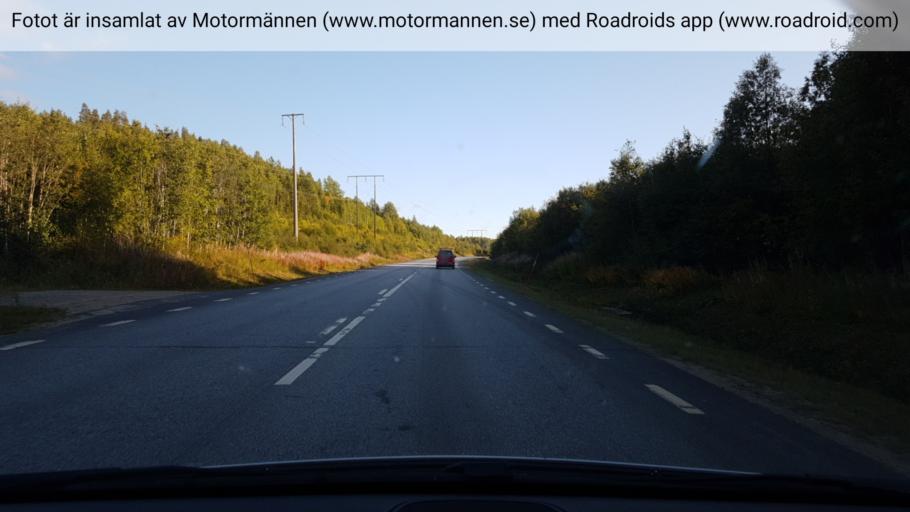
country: SE
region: Vaesterbotten
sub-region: Vannas Kommun
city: Vaennaes
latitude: 63.9938
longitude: 19.7303
